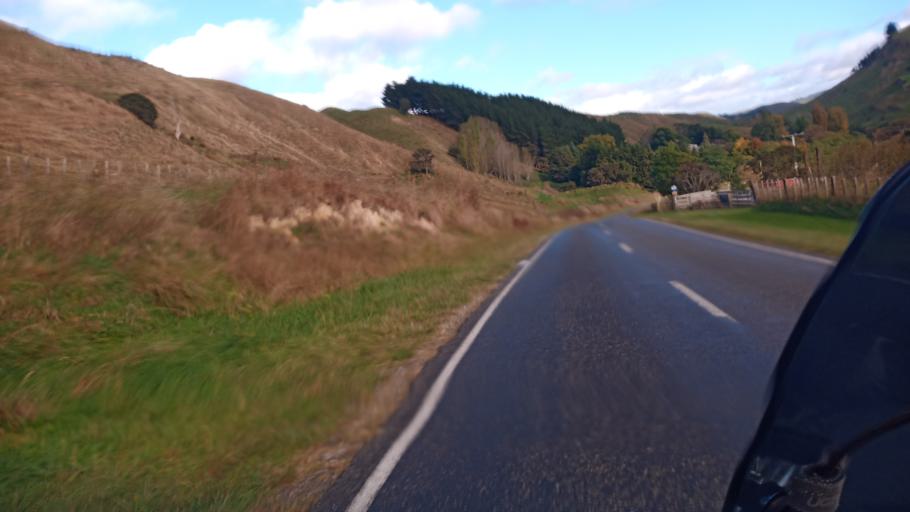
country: NZ
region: Gisborne
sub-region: Gisborne District
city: Gisborne
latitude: -38.5401
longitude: 177.5898
